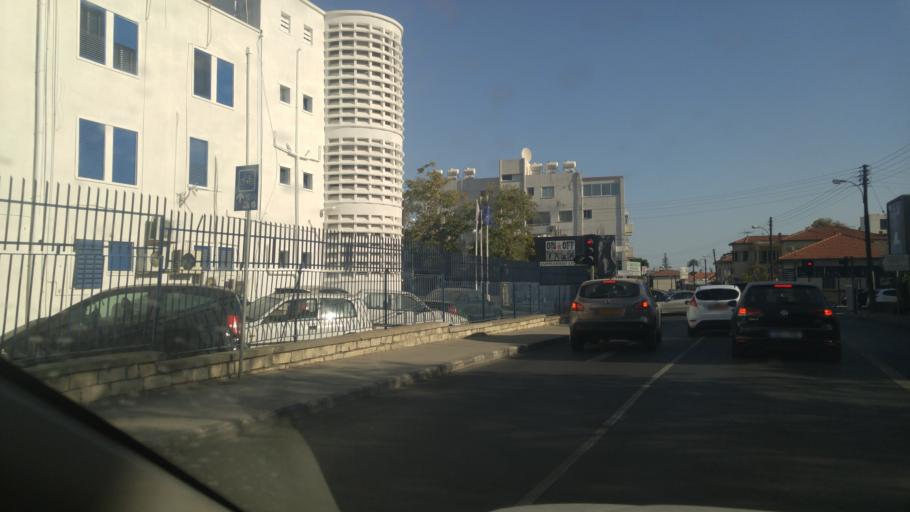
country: CY
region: Limassol
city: Limassol
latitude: 34.6783
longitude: 33.0375
